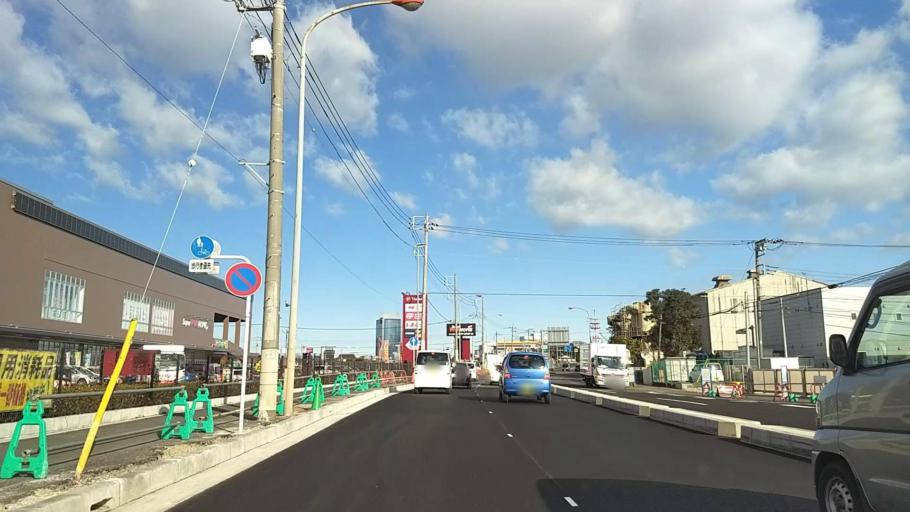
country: JP
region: Kanagawa
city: Atsugi
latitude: 35.4095
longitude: 139.3616
